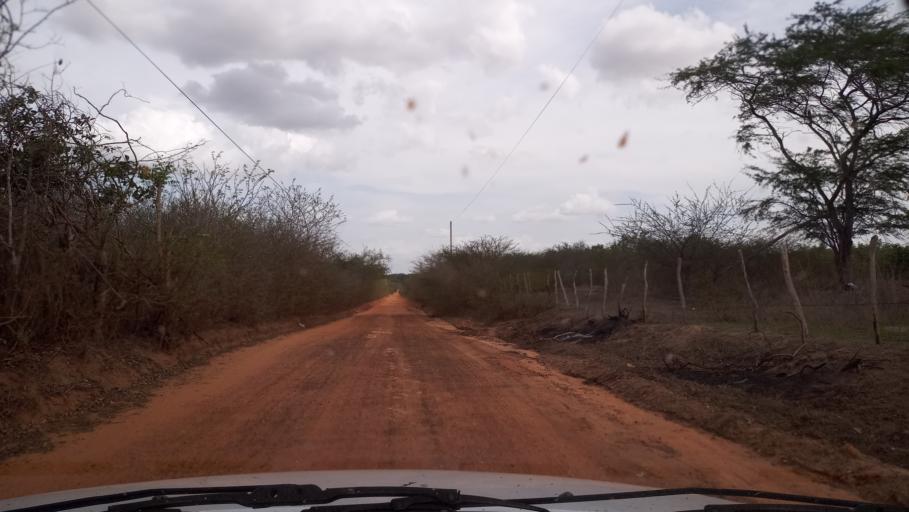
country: BR
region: Rio Grande do Norte
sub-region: Joao Camara
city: Joao Camara
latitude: -5.4988
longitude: -35.8261
